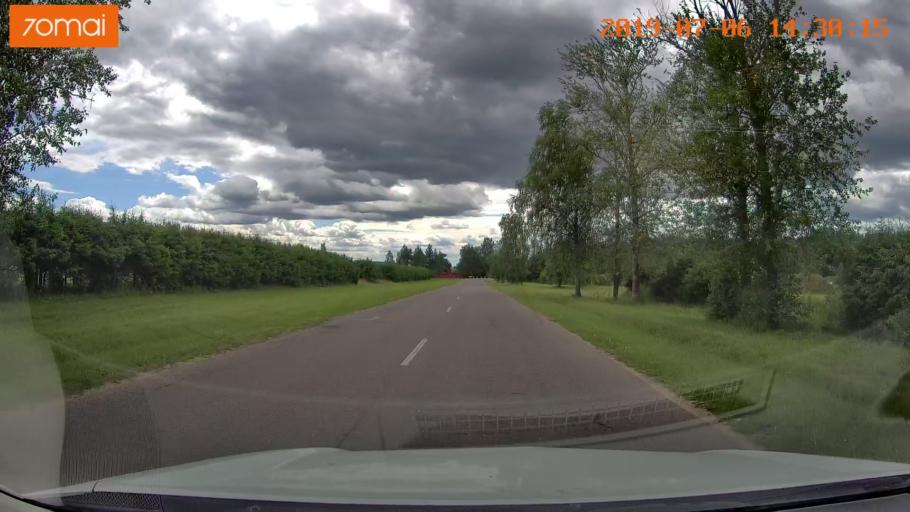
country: BY
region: Minsk
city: Ivyanyets
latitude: 53.9252
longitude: 26.7876
